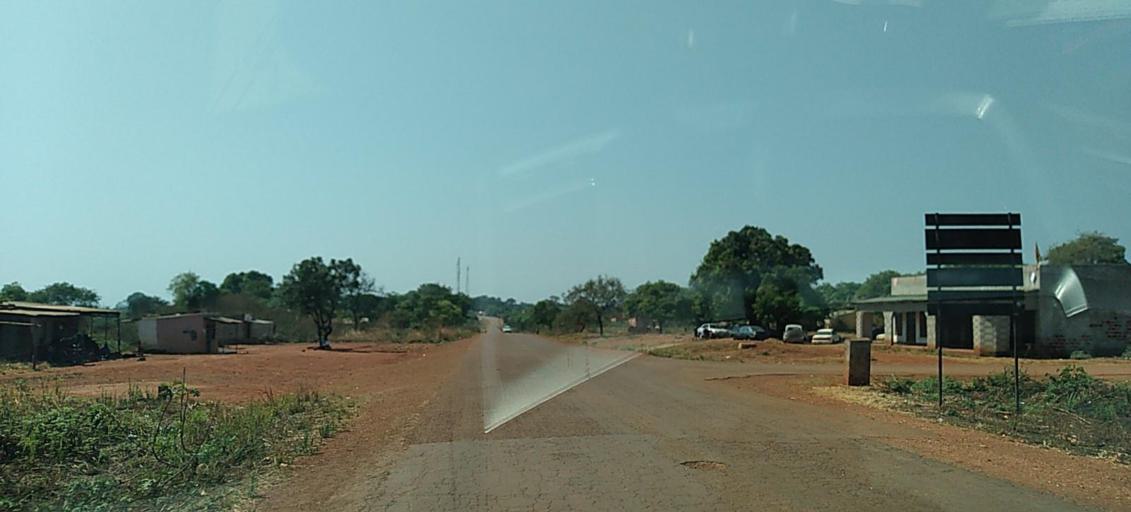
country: ZM
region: North-Western
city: Solwezi
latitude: -12.1013
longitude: 25.4918
